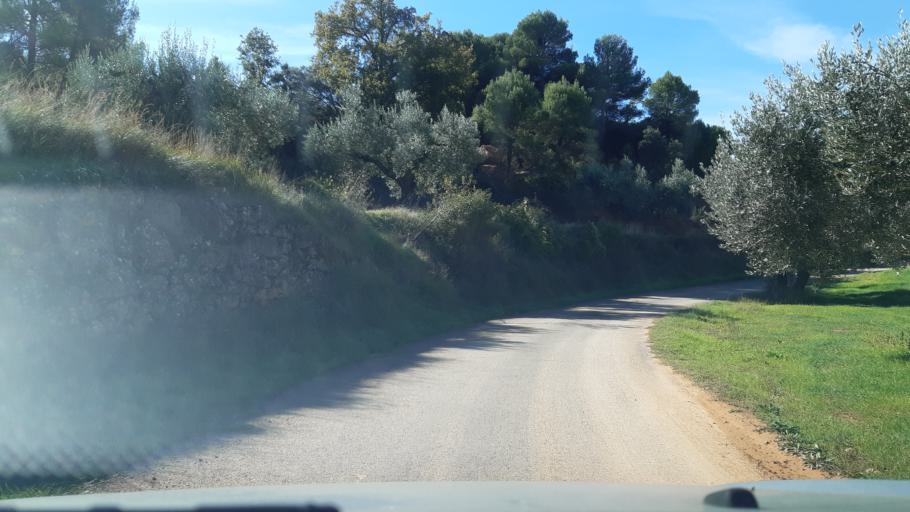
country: ES
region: Aragon
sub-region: Provincia de Teruel
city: Valderrobres
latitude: 40.8360
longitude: 0.1956
